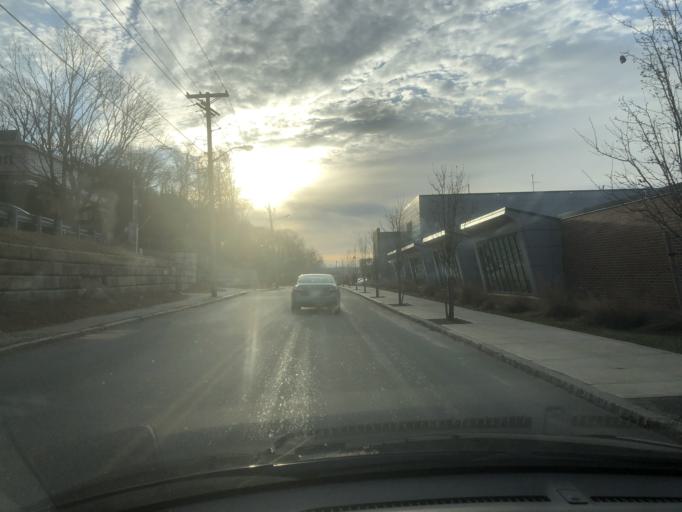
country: US
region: Massachusetts
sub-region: Essex County
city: Lawrence
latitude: 42.7106
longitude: -71.1498
